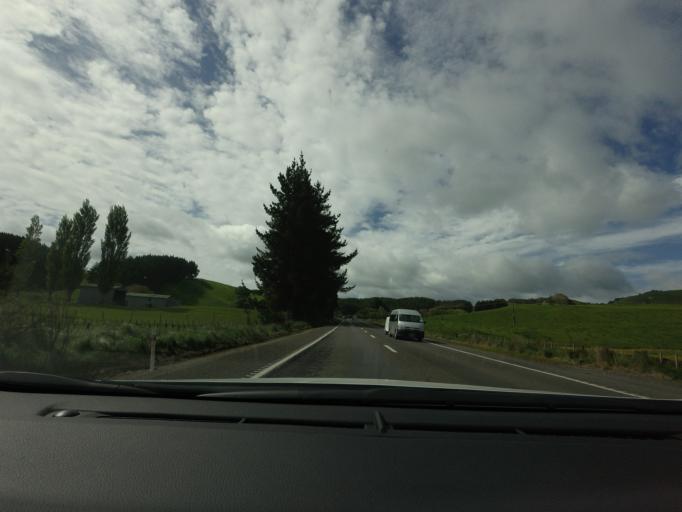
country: NZ
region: Bay of Plenty
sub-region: Rotorua District
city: Rotorua
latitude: -38.2757
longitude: 176.3376
